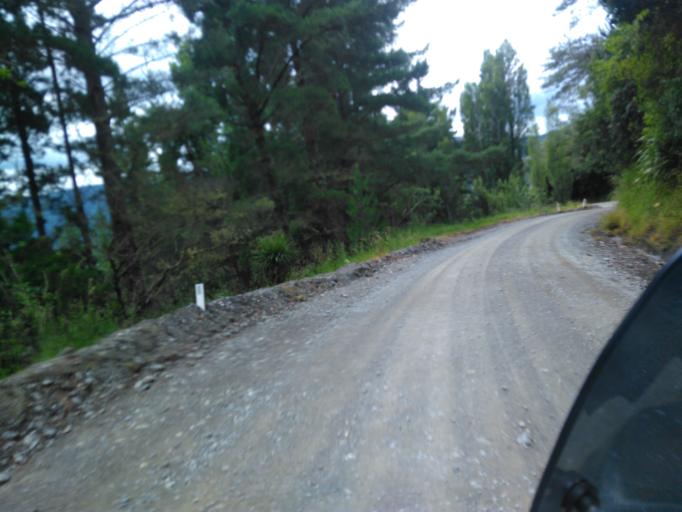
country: NZ
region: Gisborne
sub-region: Gisborne District
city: Gisborne
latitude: -38.0531
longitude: 178.1081
